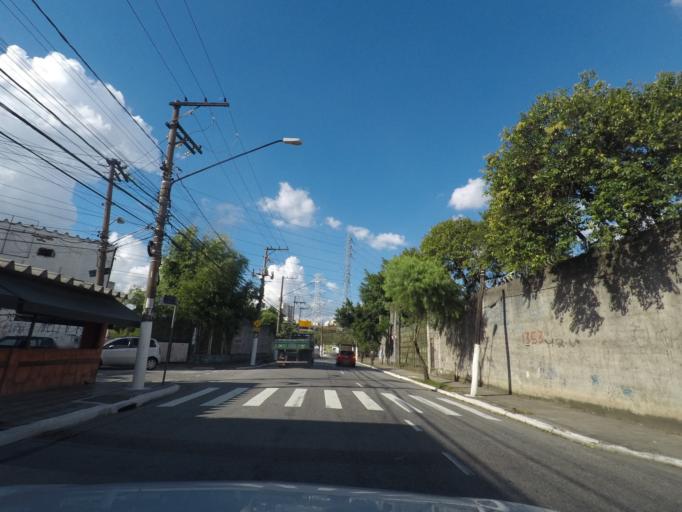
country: BR
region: Sao Paulo
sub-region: Sao Paulo
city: Sao Paulo
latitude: -23.5043
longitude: -46.6861
